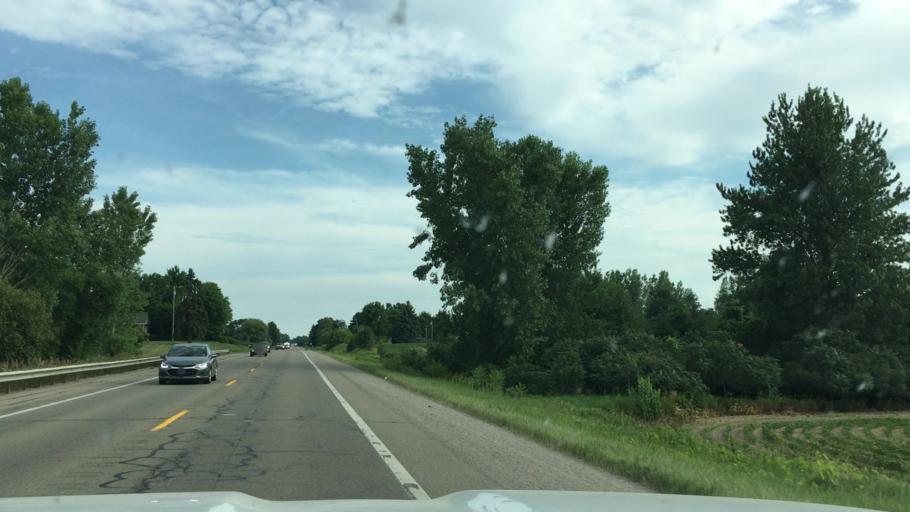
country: US
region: Michigan
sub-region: Lapeer County
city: Imlay City
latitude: 43.1223
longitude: -83.0731
